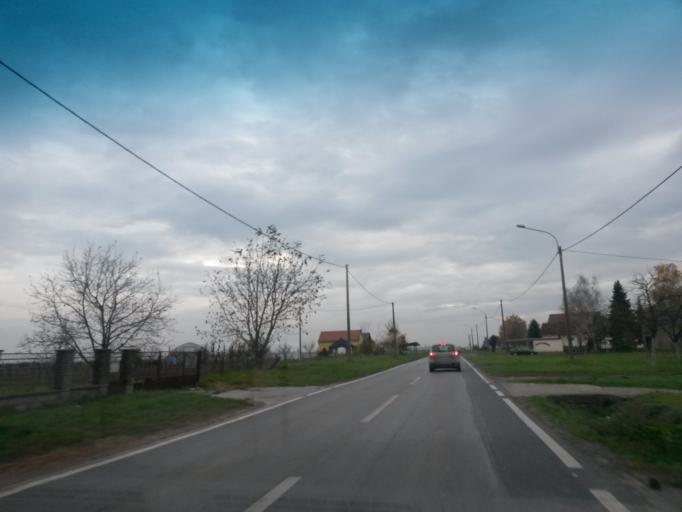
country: HR
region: Vukovarsko-Srijemska
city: Trpinja
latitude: 45.4063
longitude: 18.9105
